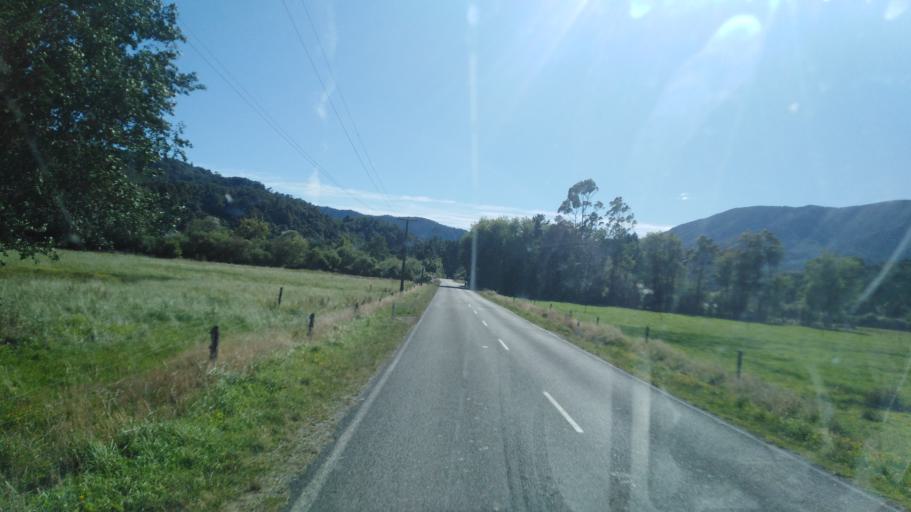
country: NZ
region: West Coast
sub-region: Buller District
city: Westport
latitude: -41.5316
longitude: 171.9636
